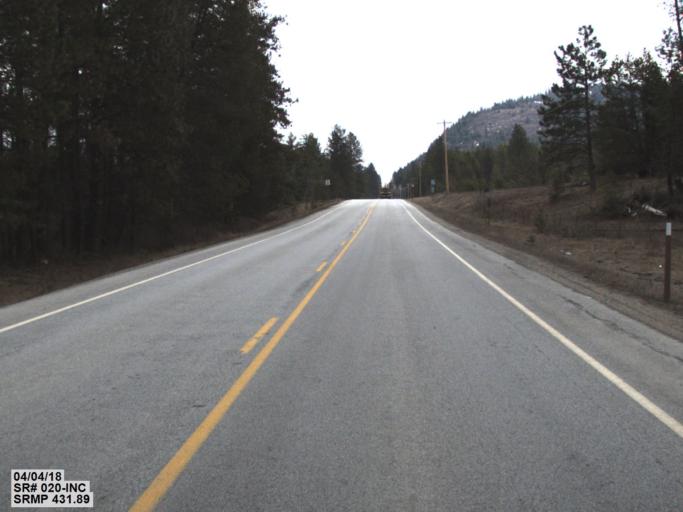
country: US
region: Washington
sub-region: Pend Oreille County
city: Newport
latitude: 48.2238
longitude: -117.1222
